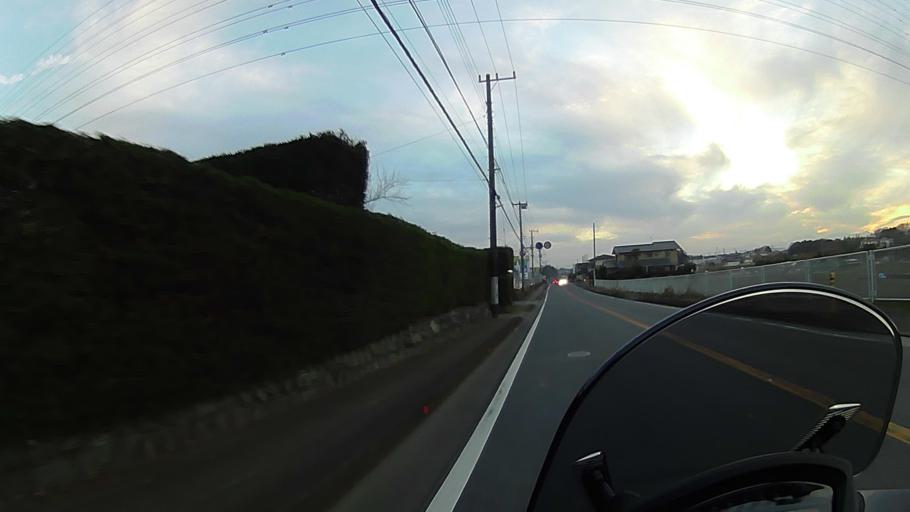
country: JP
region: Kanagawa
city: Atsugi
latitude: 35.4130
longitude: 139.4171
